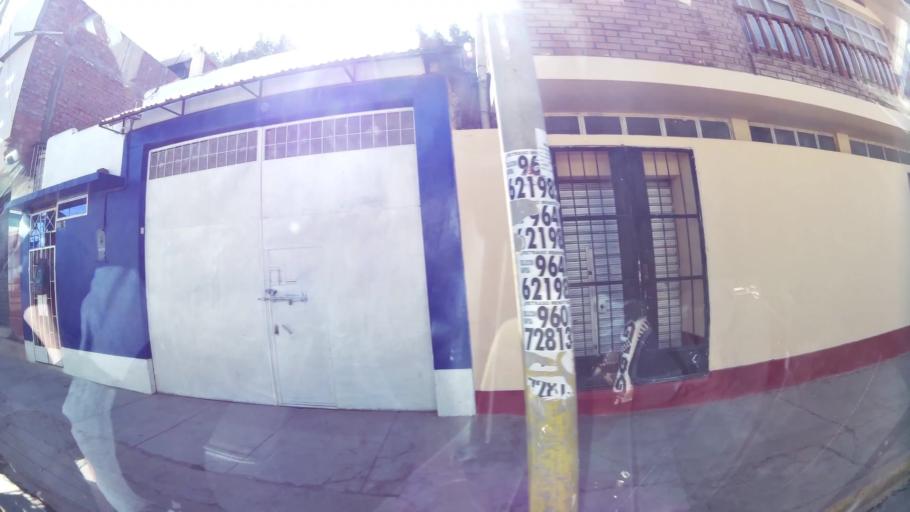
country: PE
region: Junin
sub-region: Provincia de Concepcion
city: Concepcion
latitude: -11.9147
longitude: -75.3143
